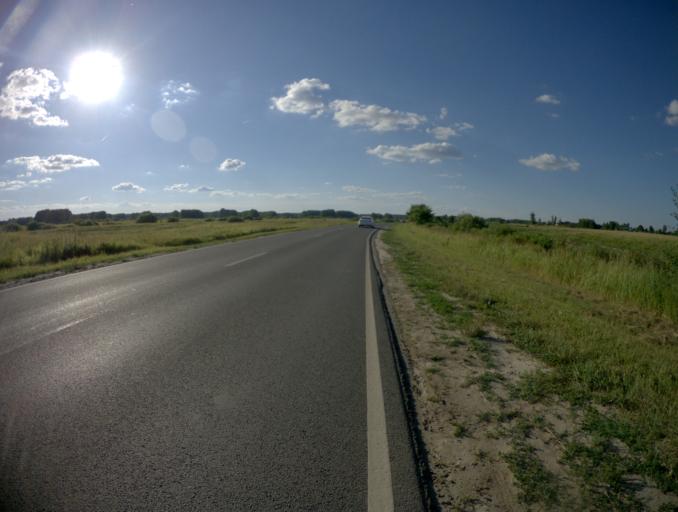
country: RU
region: Nizjnij Novgorod
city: Pavlovo
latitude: 55.9784
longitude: 43.0505
